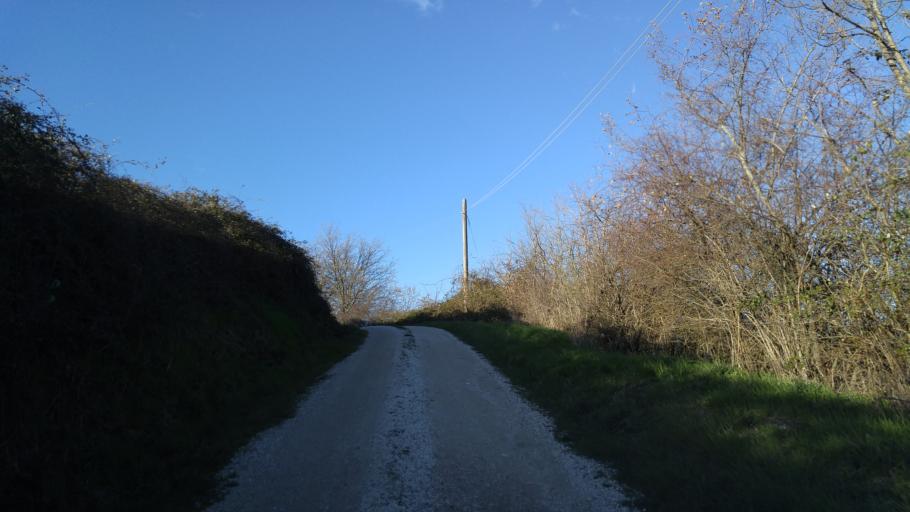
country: IT
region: The Marches
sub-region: Provincia di Pesaro e Urbino
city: San Costanzo
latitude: 43.7487
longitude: 13.0270
